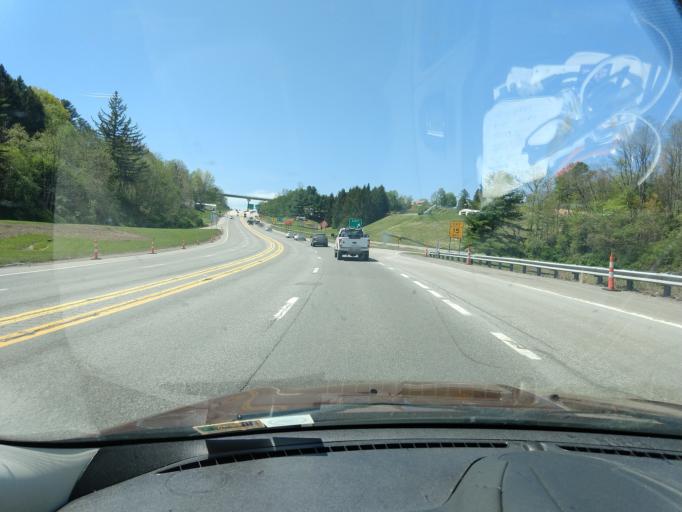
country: US
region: West Virginia
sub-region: Raleigh County
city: MacArthur
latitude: 37.7628
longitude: -81.2087
